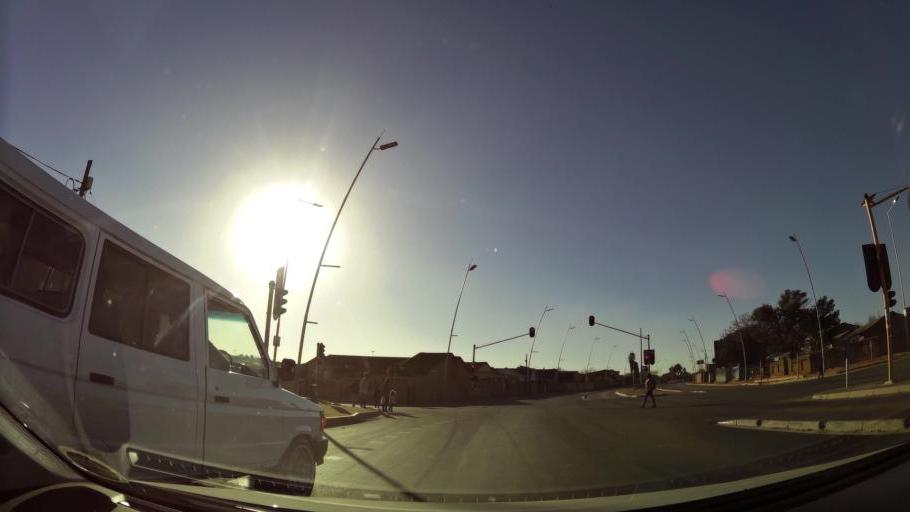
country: ZA
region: Gauteng
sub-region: Ekurhuleni Metropolitan Municipality
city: Tembisa
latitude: -26.0113
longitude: 28.2177
